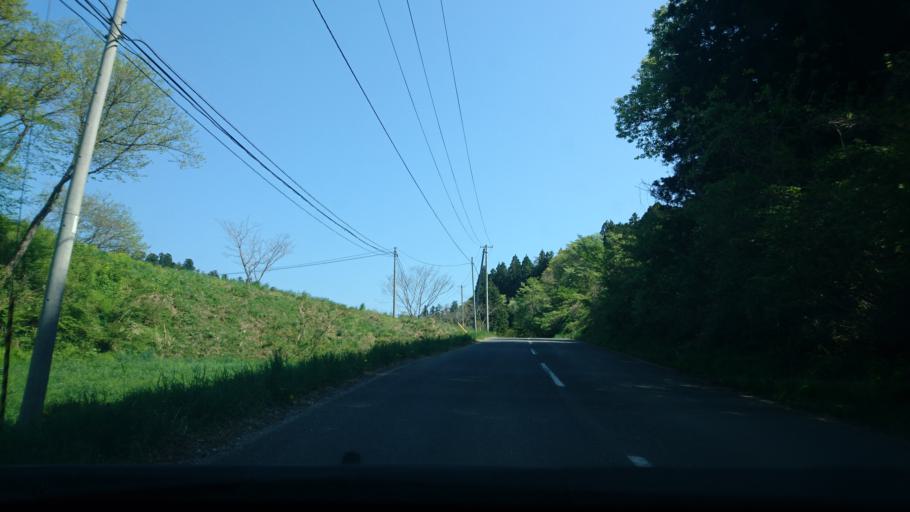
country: JP
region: Iwate
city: Ichinoseki
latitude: 38.9388
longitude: 141.2753
